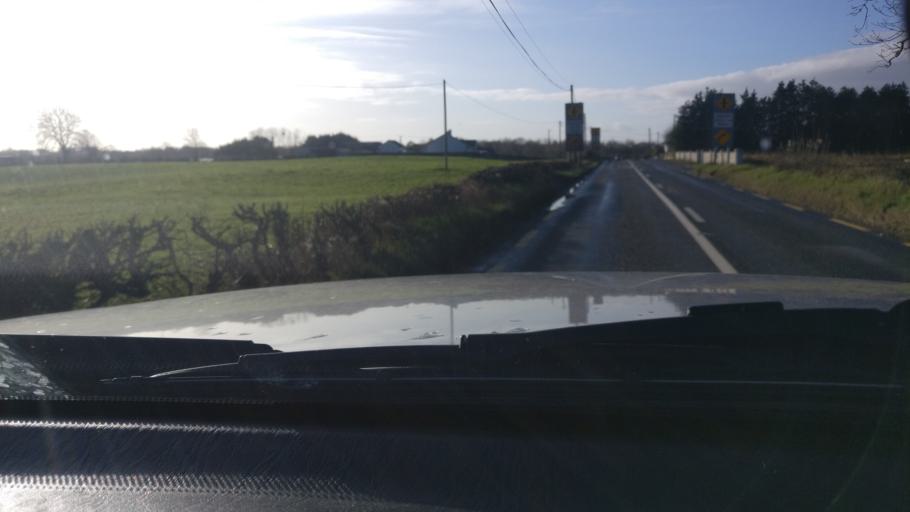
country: IE
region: Leinster
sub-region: An Longfort
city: Ballymahon
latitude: 53.5762
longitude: -7.7412
